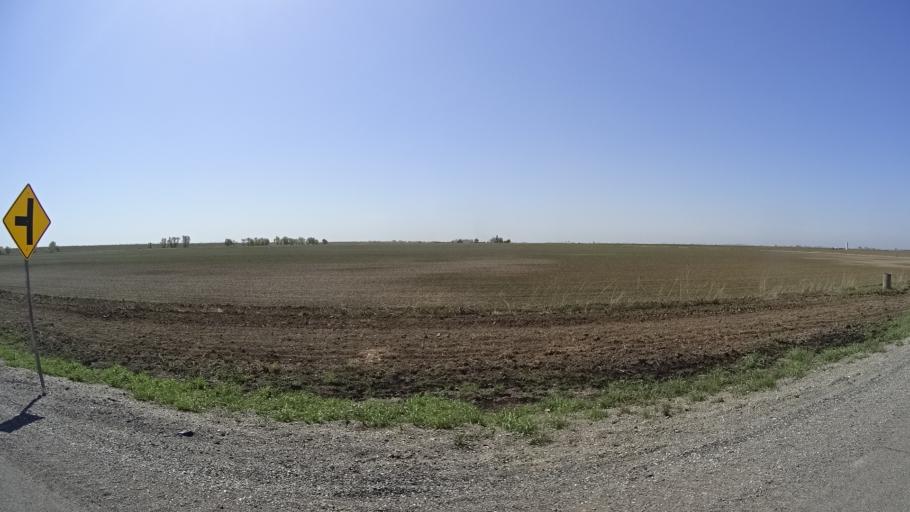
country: US
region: California
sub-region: Glenn County
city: Willows
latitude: 39.5218
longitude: -122.0351
